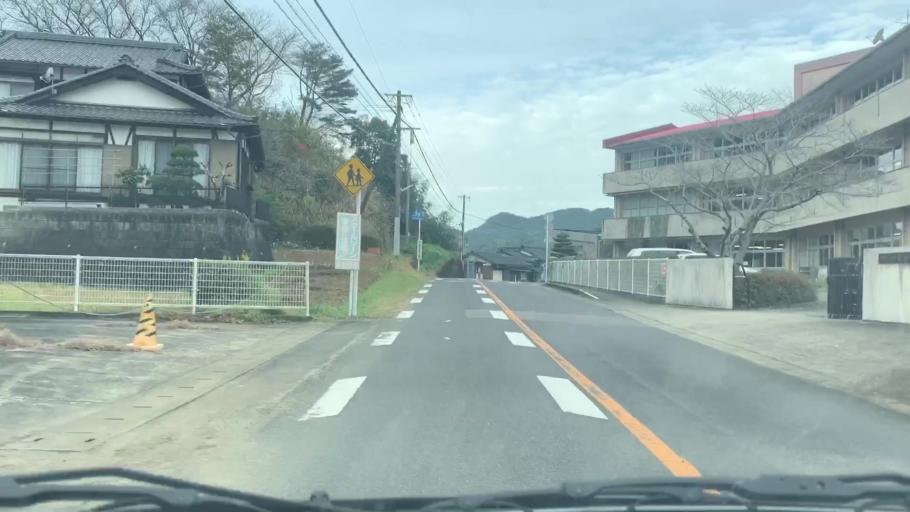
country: JP
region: Saga Prefecture
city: Takeocho-takeo
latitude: 33.1928
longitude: 129.9645
